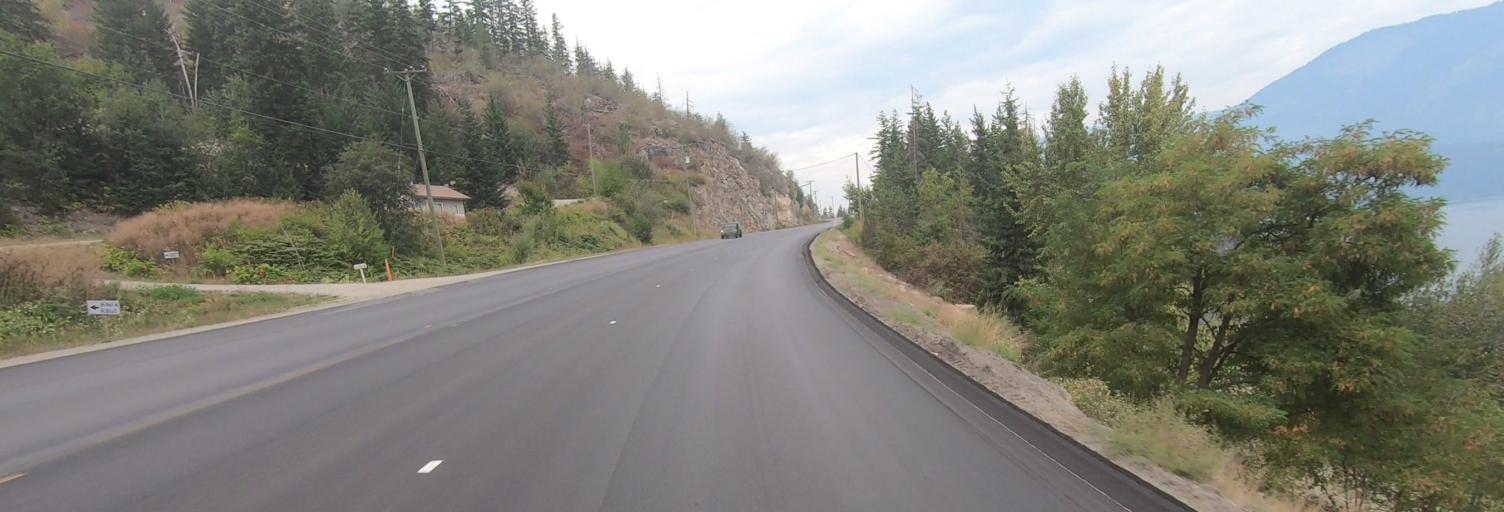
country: CA
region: British Columbia
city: Salmon Arm
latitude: 50.7508
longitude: -119.3254
